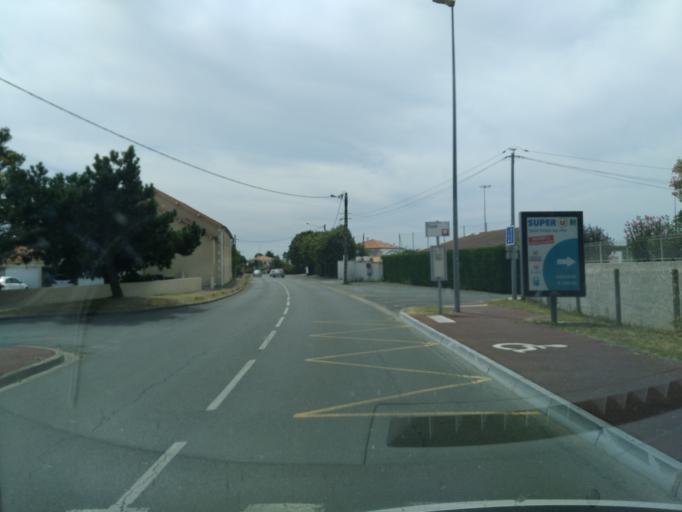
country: FR
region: Poitou-Charentes
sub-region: Departement de la Charente-Maritime
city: Saint-Palais-sur-Mer
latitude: 45.6519
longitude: -1.0801
